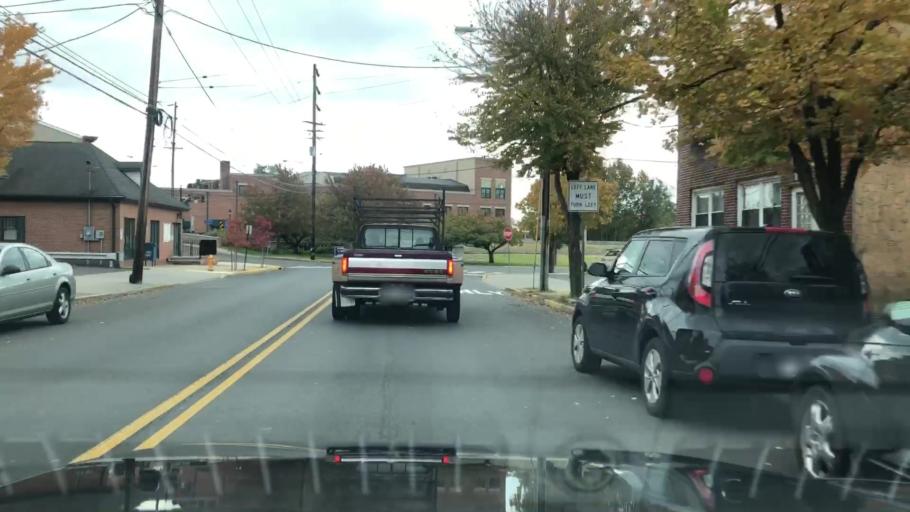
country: US
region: Pennsylvania
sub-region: Bucks County
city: Bristol
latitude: 40.0976
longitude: -74.8610
